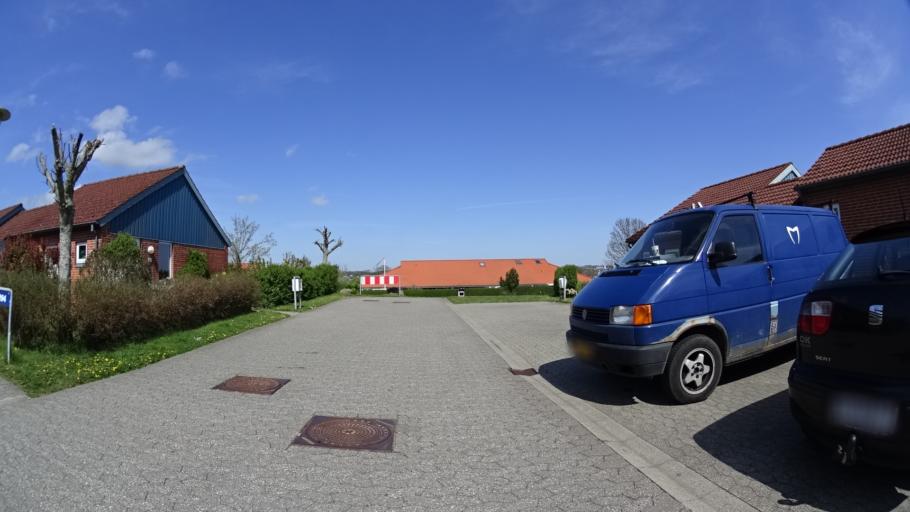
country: DK
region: Central Jutland
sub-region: Arhus Kommune
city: Stavtrup
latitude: 56.1312
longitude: 10.1114
